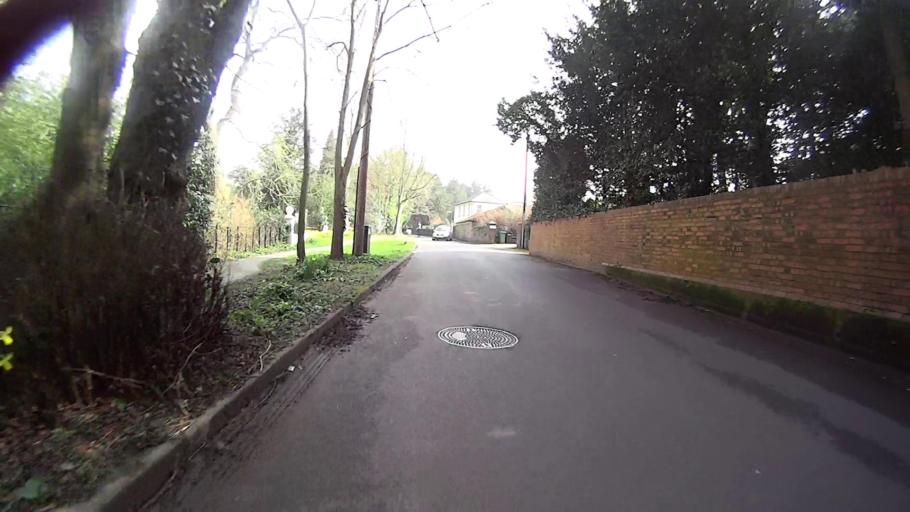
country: GB
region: England
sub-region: Surrey
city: Mickleham
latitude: 51.2539
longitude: -0.3273
